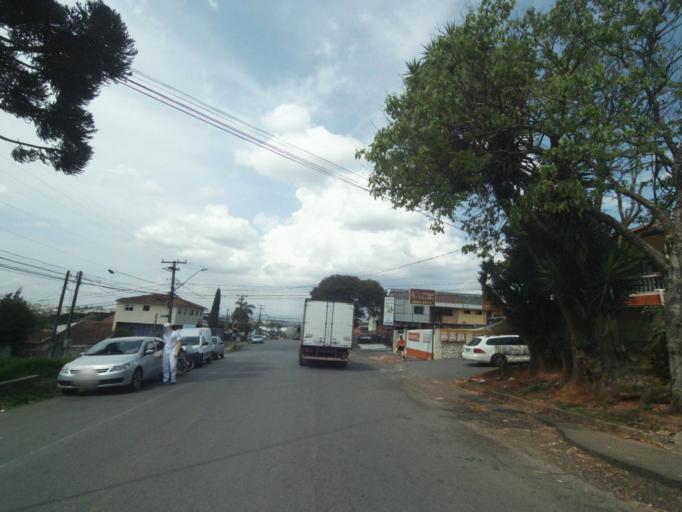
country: BR
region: Parana
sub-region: Pinhais
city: Pinhais
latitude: -25.3996
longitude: -49.2012
